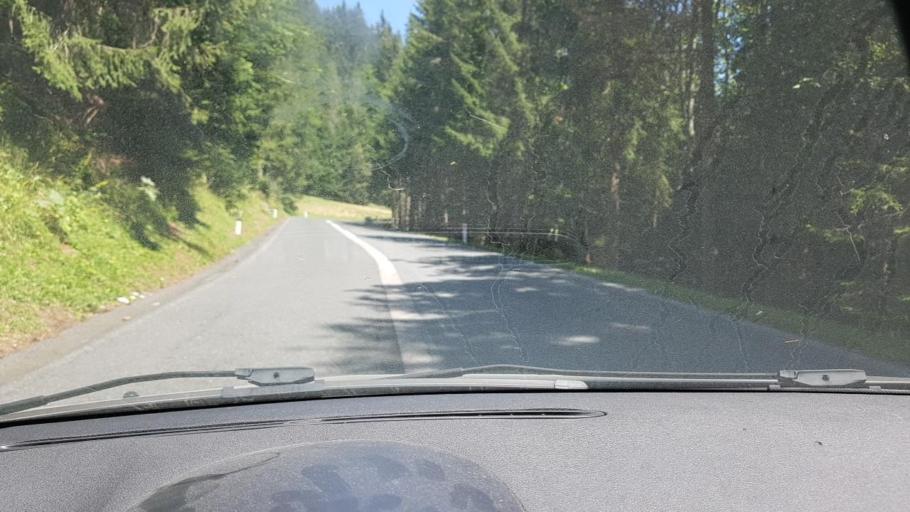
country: SI
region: Jezersko
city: Zgornje Jezersko
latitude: 46.4199
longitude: 14.5313
